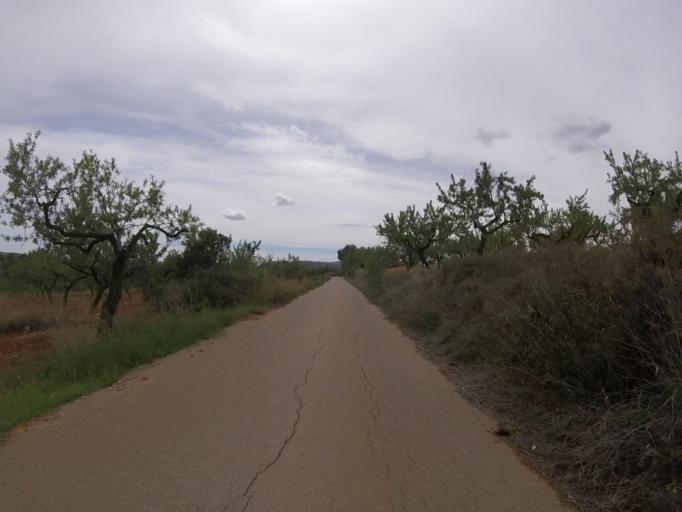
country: ES
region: Valencia
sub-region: Provincia de Castello
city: Benlloch
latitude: 40.1829
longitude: -0.0083
